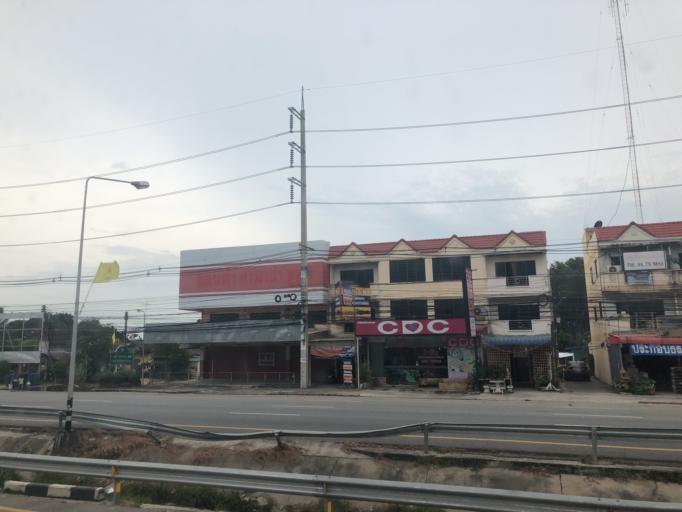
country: TH
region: Chon Buri
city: Bang Lamung
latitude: 13.0172
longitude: 100.9318
